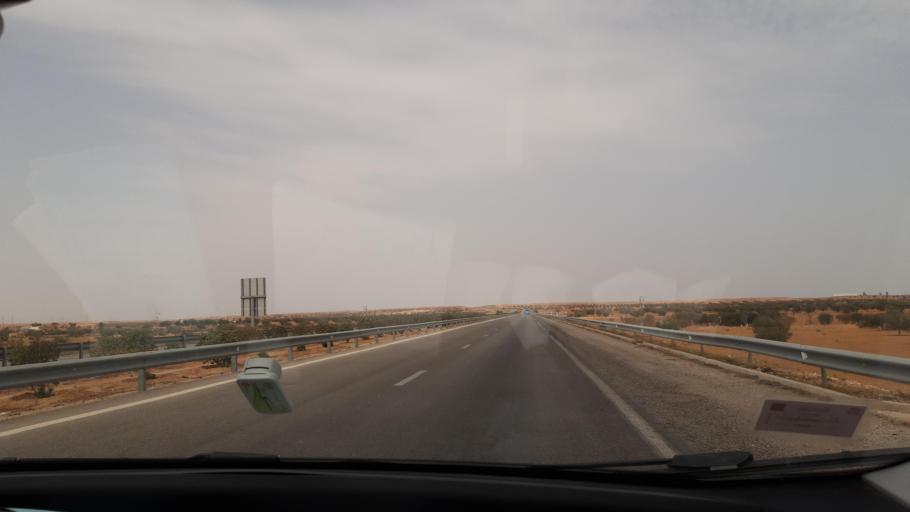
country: TN
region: Safaqis
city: Sfax
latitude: 34.7413
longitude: 10.5976
